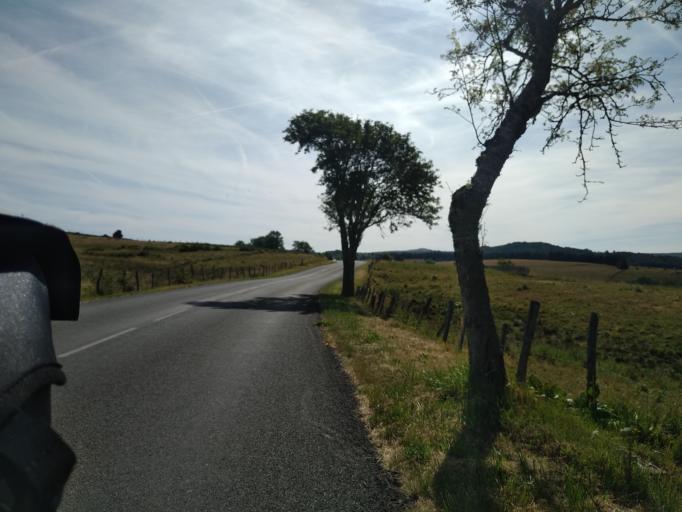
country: FR
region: Auvergne
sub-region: Departement du Cantal
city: Chaudes-Aigues
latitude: 44.6729
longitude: 3.0622
